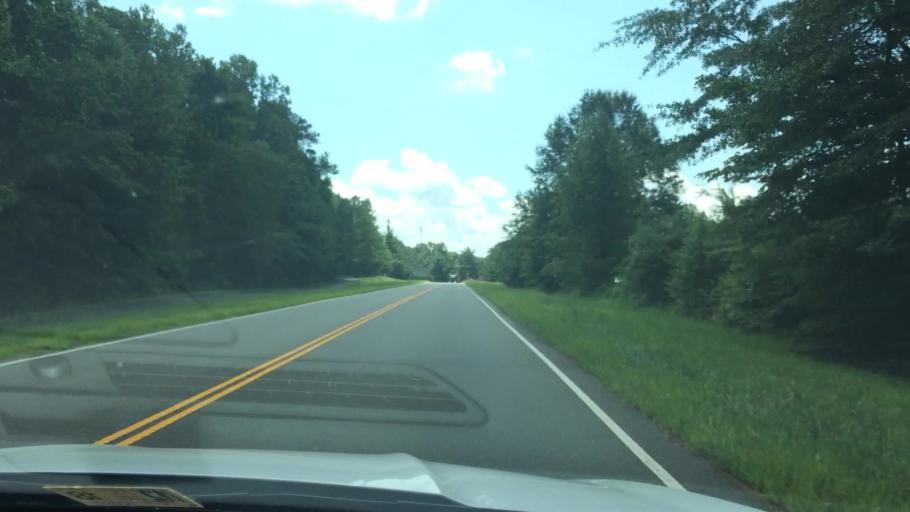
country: US
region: Virginia
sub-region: James City County
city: Williamsburg
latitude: 37.2939
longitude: -76.7345
